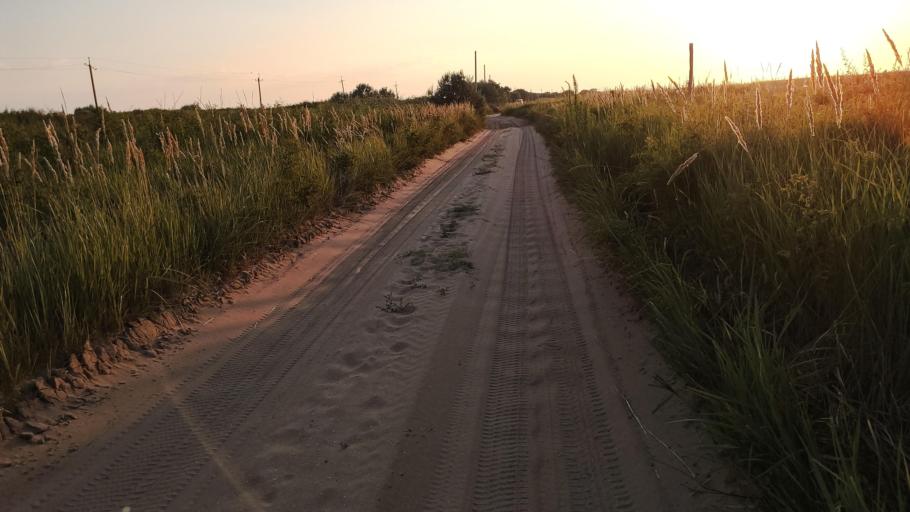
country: RU
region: Krasnodarskiy
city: Blagovetschenskaya
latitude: 45.0682
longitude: 37.0315
